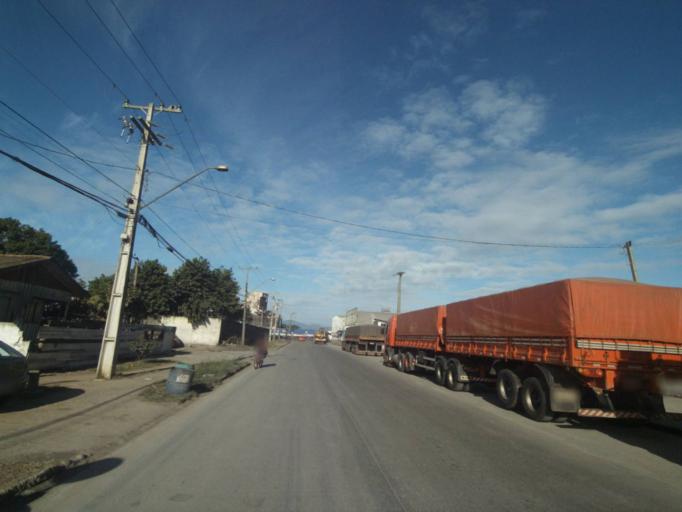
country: BR
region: Parana
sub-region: Paranagua
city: Paranagua
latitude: -25.5131
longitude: -48.5234
